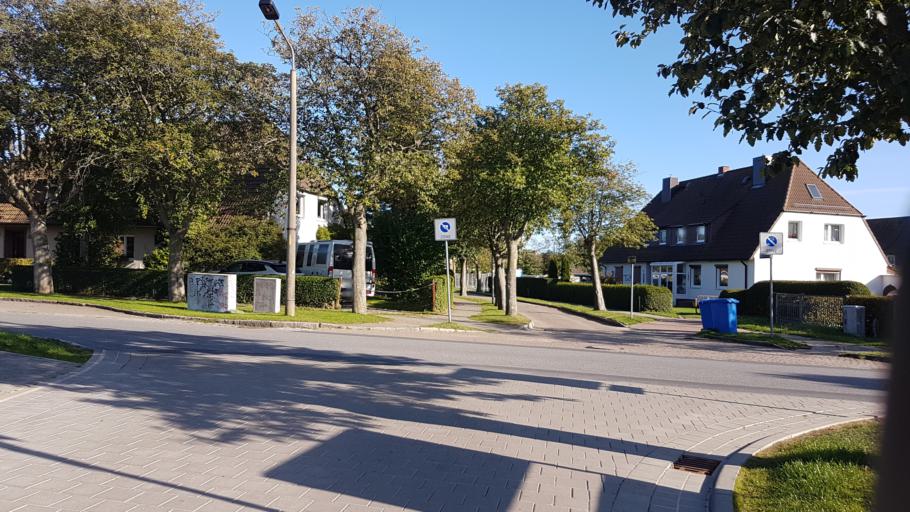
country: DE
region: Mecklenburg-Vorpommern
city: Dranske
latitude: 54.6282
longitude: 13.2283
